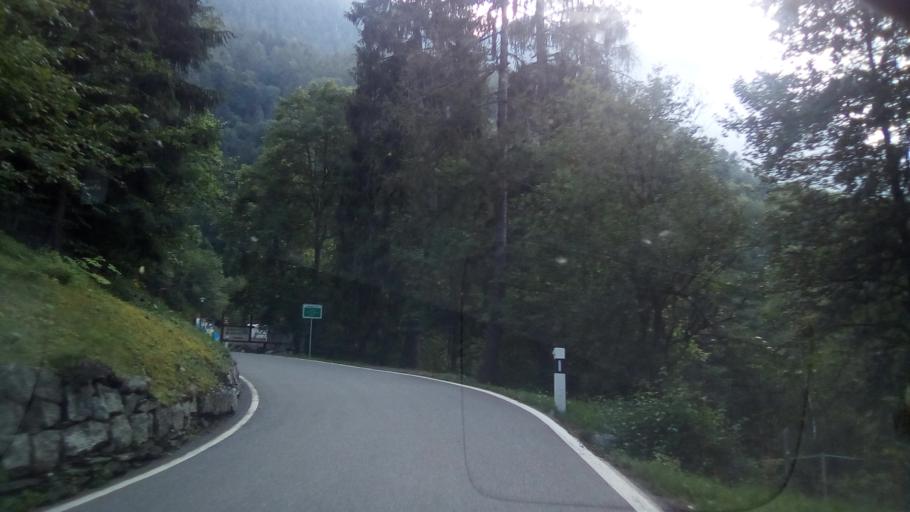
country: CH
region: Valais
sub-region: Martigny District
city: Martigny-Combe
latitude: 46.0706
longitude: 7.0724
